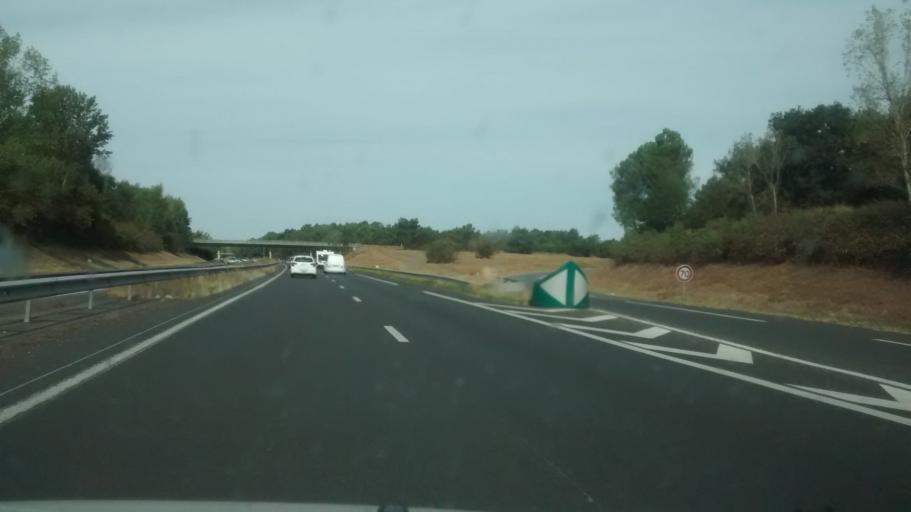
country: FR
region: Aquitaine
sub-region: Departement de la Gironde
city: La Reole
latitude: 44.5063
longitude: -0.0426
